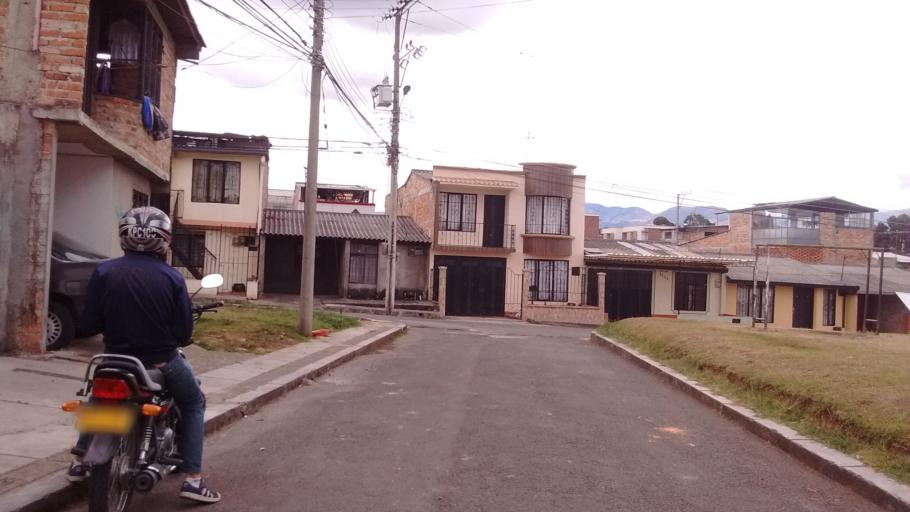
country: CO
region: Cauca
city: Popayan
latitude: 2.4889
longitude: -76.5826
